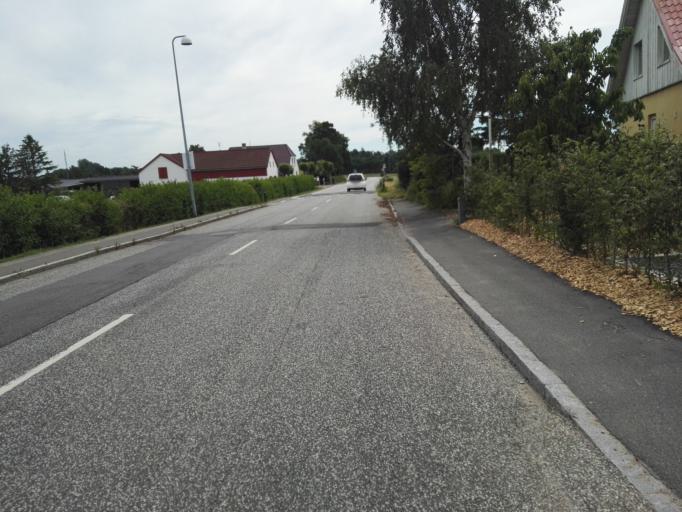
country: DK
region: Capital Region
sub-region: Hillerod Kommune
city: Skaevinge
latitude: 55.9025
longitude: 12.1514
